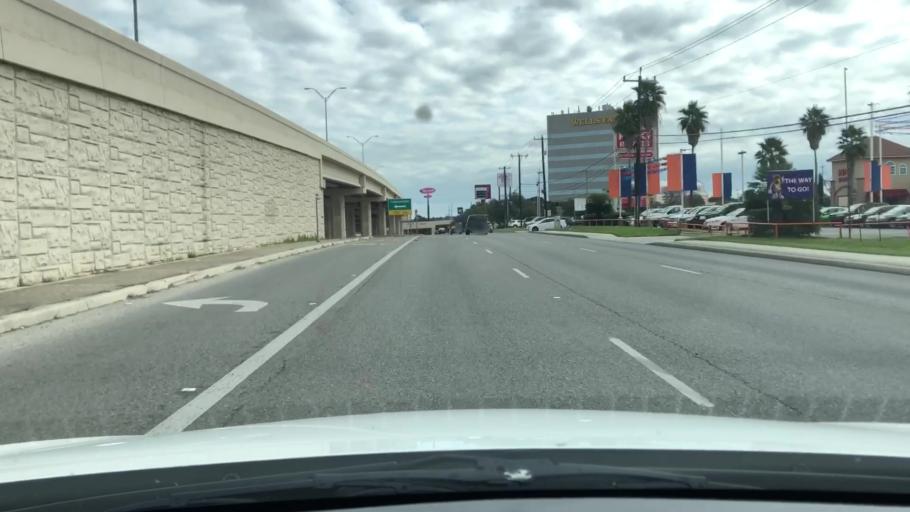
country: US
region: Texas
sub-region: Bexar County
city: Leon Valley
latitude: 29.4866
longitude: -98.6076
